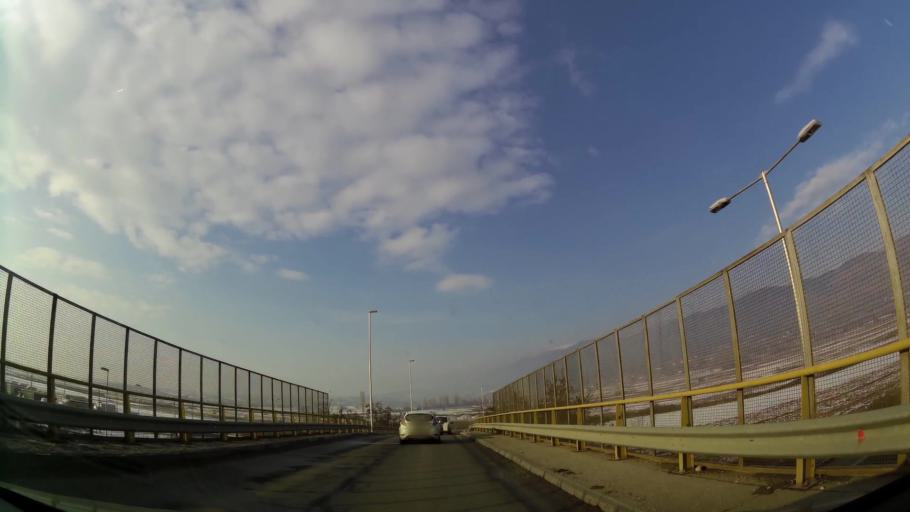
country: MK
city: Creshevo
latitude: 42.0319
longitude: 21.5116
